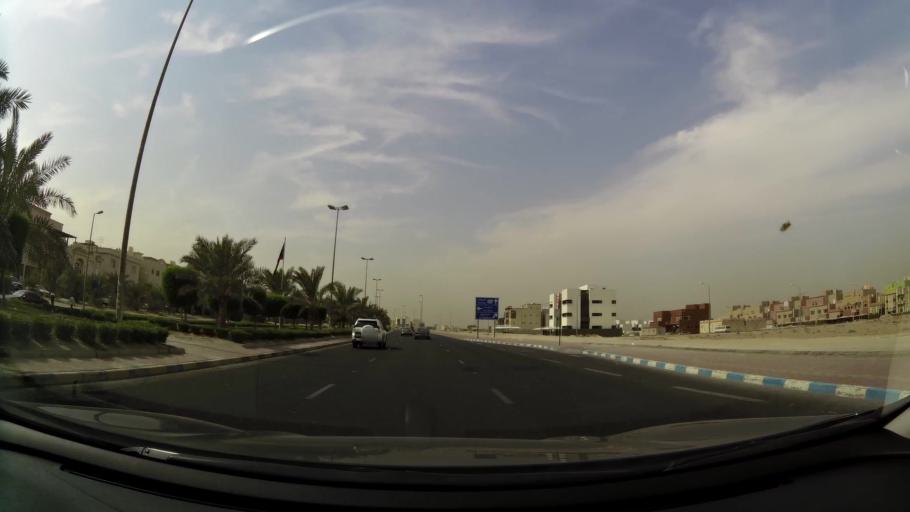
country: KW
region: Al Farwaniyah
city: Janub as Surrah
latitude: 29.2858
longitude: 47.9975
